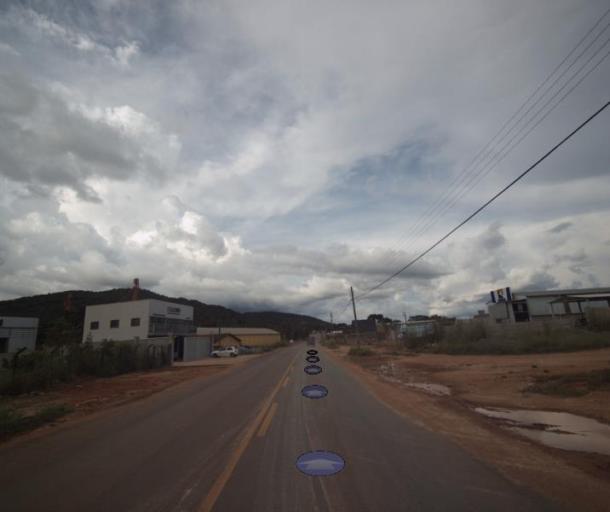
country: BR
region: Goias
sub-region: Niquelandia
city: Niquelandia
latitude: -14.4696
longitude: -48.4858
